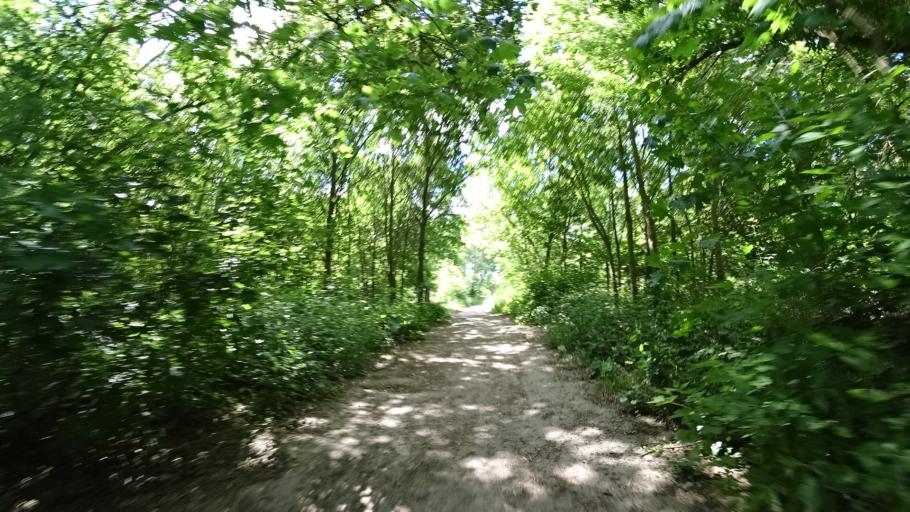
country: DE
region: Berlin
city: Lichtenrade
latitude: 52.3881
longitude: 13.3802
